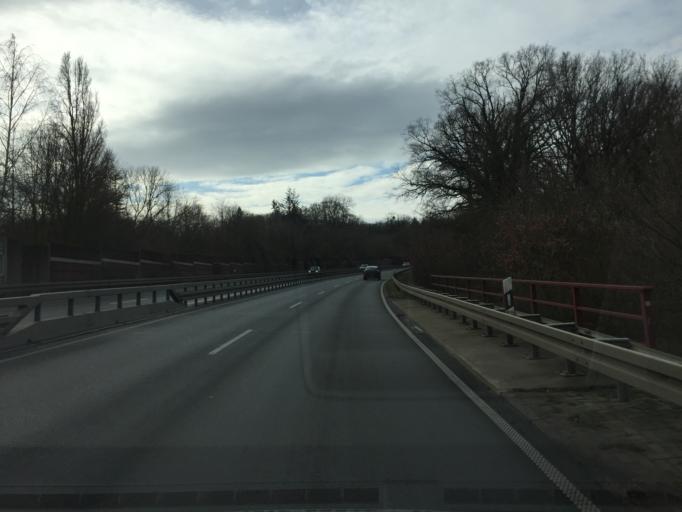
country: DE
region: Lower Saxony
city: Wennigsen
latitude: 52.2423
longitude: 9.6333
